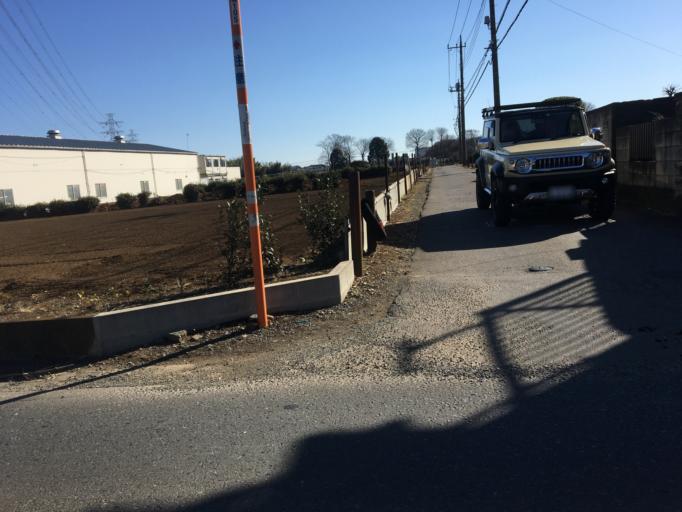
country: JP
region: Saitama
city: Oi
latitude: 35.8190
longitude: 139.5318
